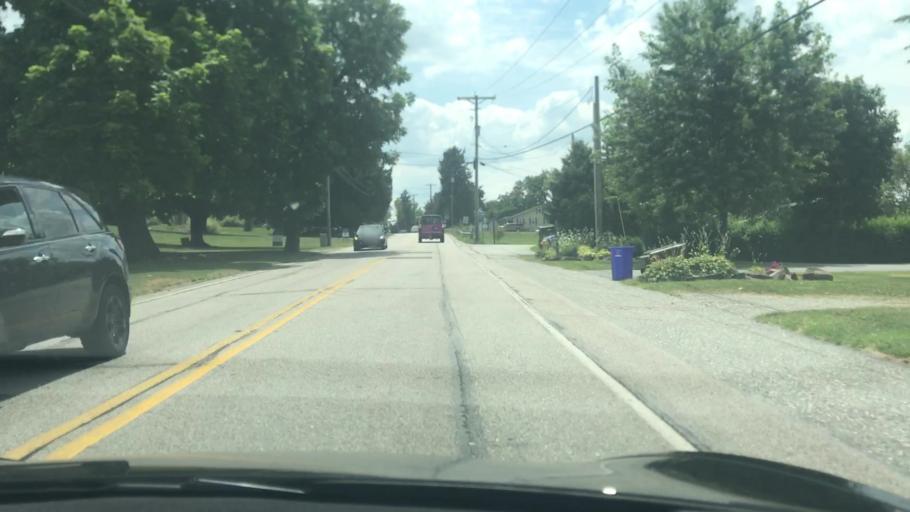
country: US
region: Pennsylvania
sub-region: York County
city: Manchester
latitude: 40.0567
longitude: -76.7659
